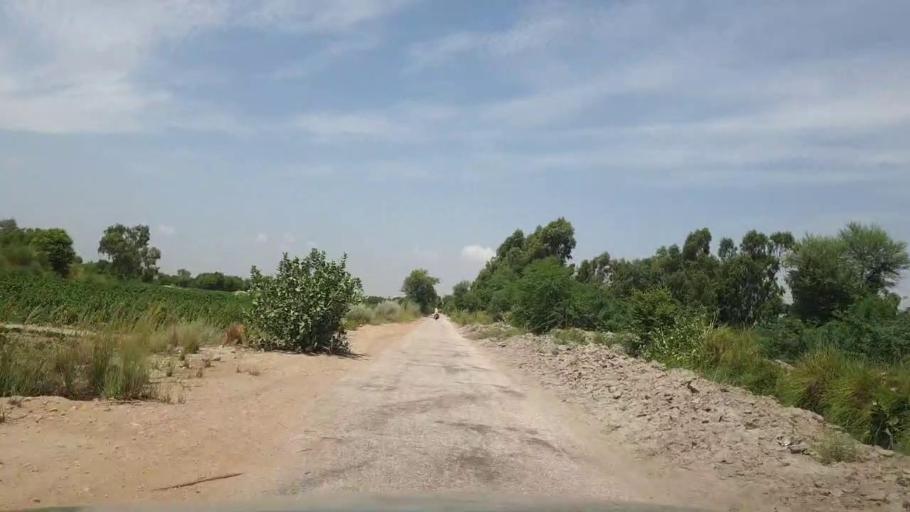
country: PK
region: Sindh
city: Bozdar
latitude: 27.0898
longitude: 69.0064
